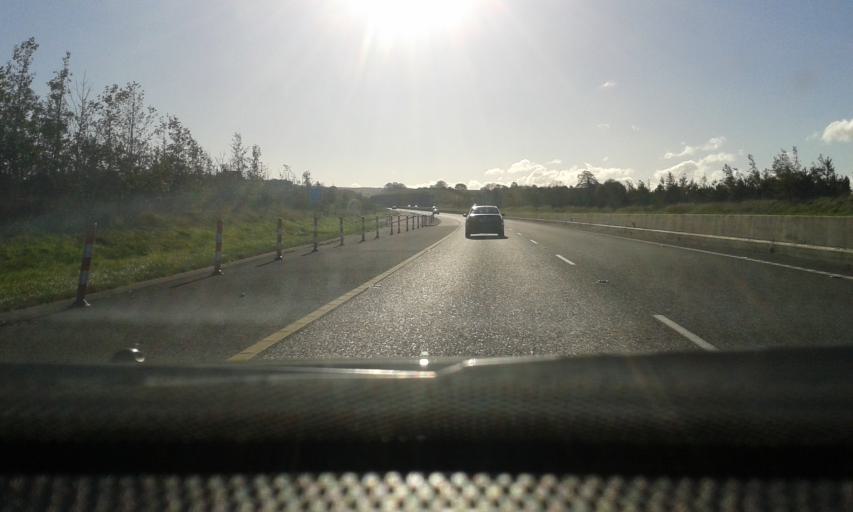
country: IE
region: Leinster
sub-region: Laois
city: Rathdowney
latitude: 52.8326
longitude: -7.5009
